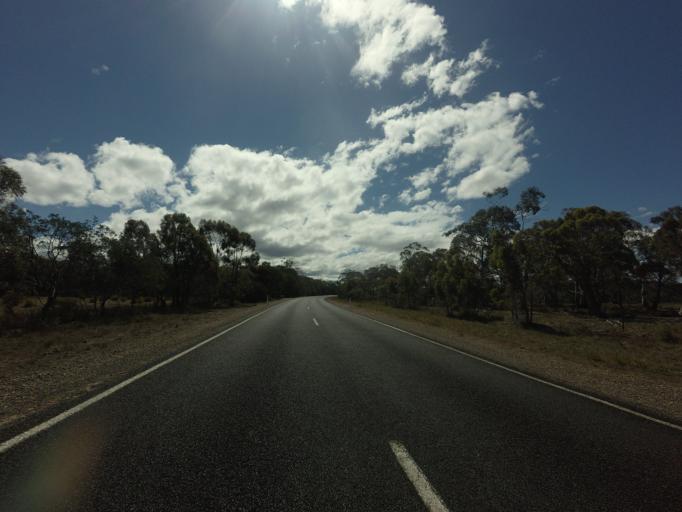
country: AU
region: Tasmania
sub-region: Break O'Day
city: St Helens
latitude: -42.0397
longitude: 148.0292
